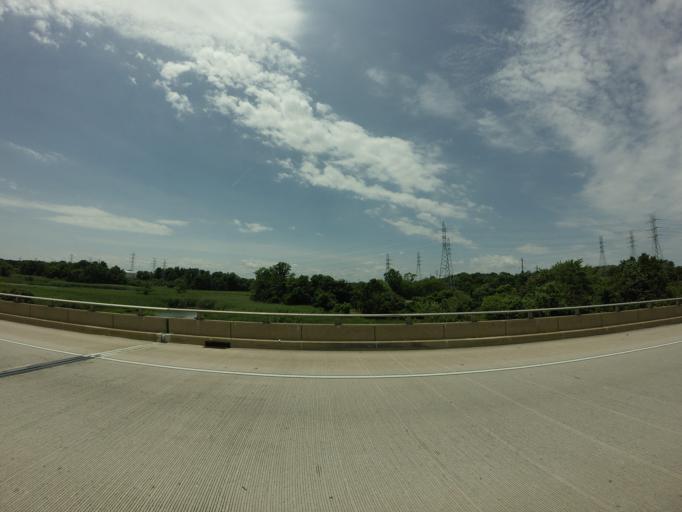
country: US
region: Maryland
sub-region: Baltimore County
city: Rosedale
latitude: 39.3060
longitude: -76.5009
